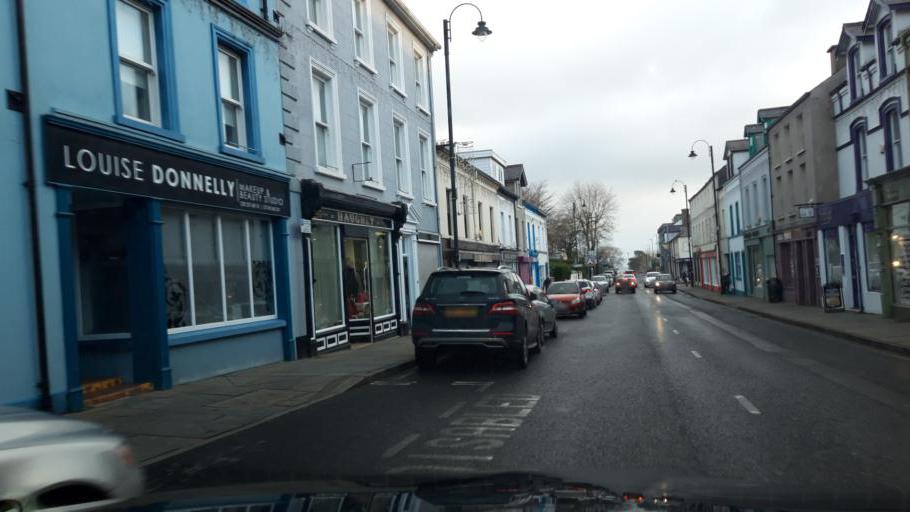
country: GB
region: Northern Ireland
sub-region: Moyle District
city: Ballycastle
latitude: 55.2019
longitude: -6.2490
